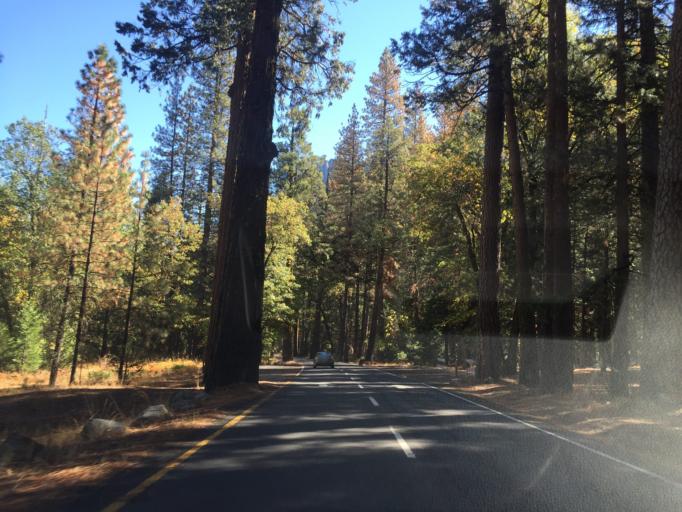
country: US
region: California
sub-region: Mariposa County
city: Yosemite Valley
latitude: 37.7216
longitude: -119.6250
